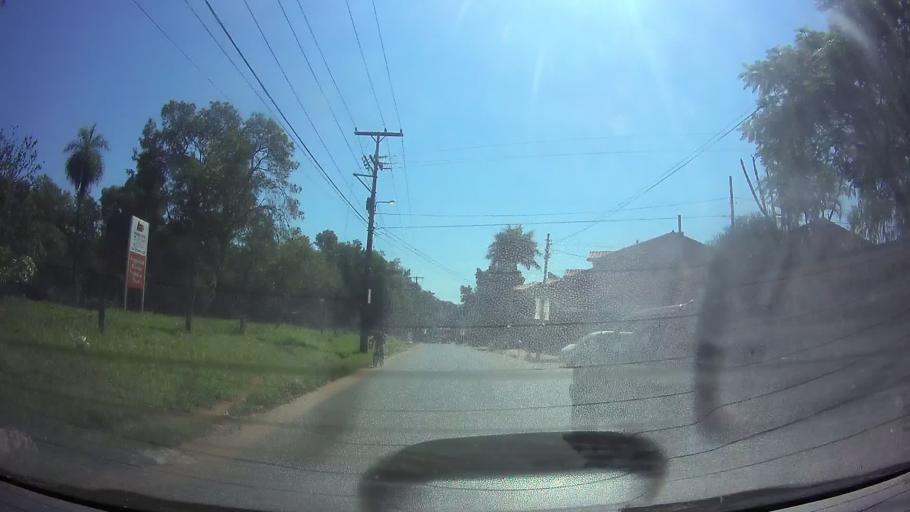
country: PY
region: Central
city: Fernando de la Mora
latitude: -25.3187
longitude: -57.5217
